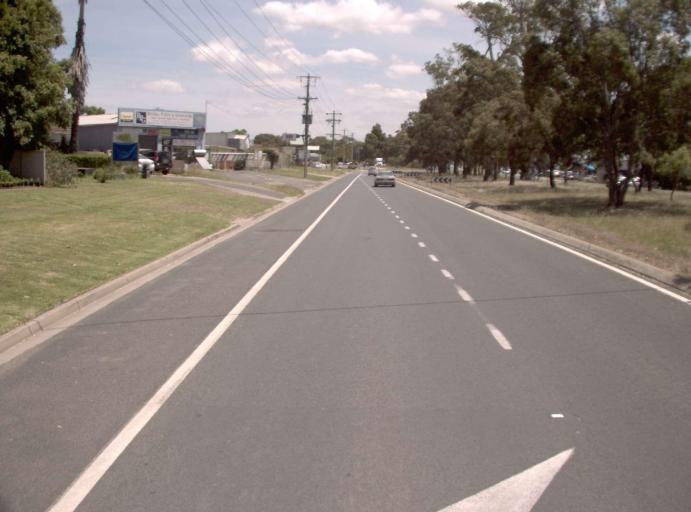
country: AU
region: Victoria
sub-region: East Gippsland
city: Bairnsdale
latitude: -37.8375
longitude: 147.5982
